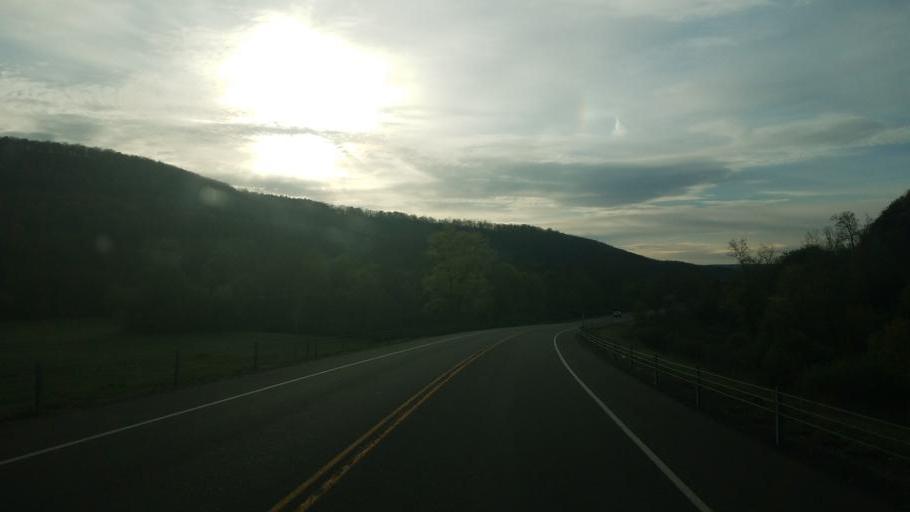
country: US
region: New York
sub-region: Steuben County
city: Hornell
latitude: 42.3445
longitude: -77.7037
